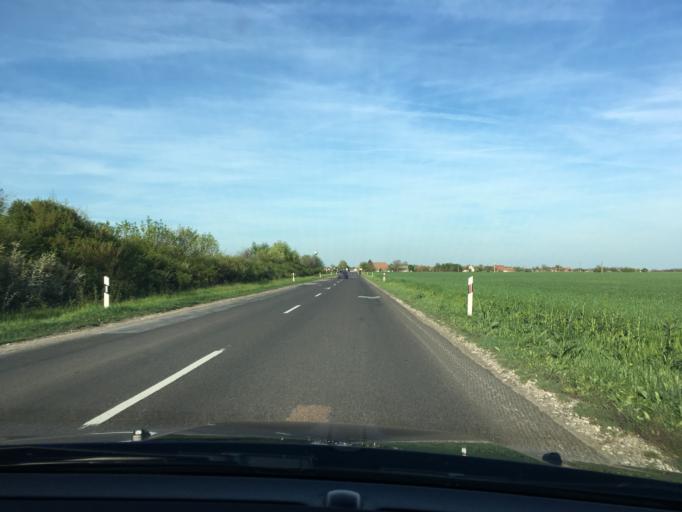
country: HU
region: Hajdu-Bihar
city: Csokmo
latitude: 47.0196
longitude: 21.2691
